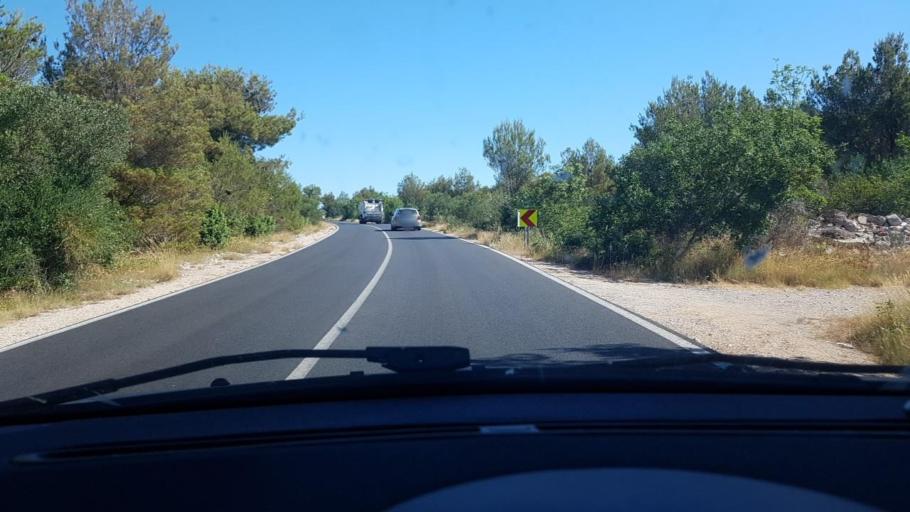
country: HR
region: Sibensko-Kniniska
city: Vodice
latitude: 43.7567
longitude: 15.8155
